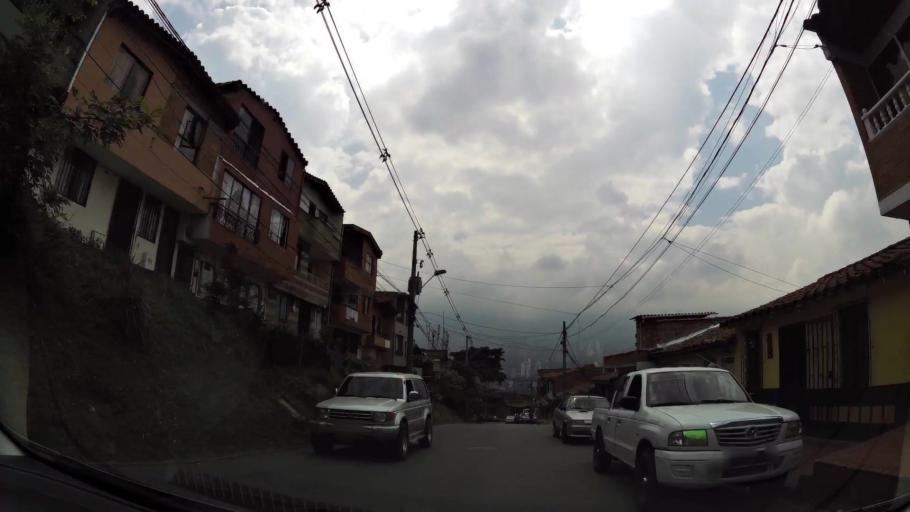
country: CO
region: Antioquia
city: Itagui
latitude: 6.1998
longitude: -75.5938
